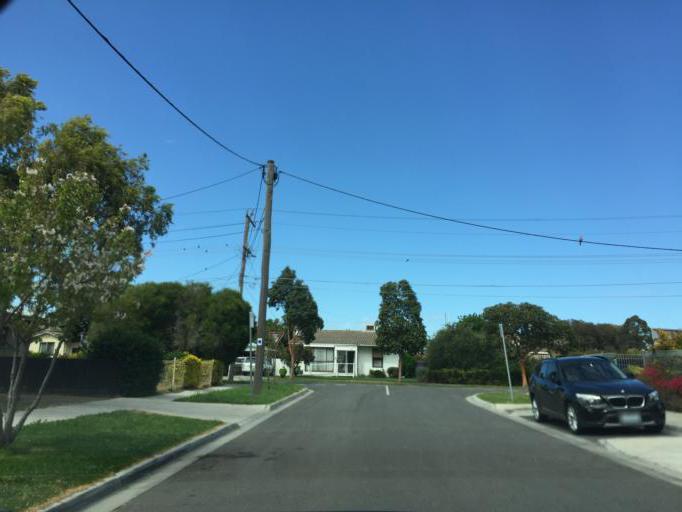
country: AU
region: Victoria
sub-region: Maribyrnong
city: Braybrook
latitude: -37.7845
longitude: 144.8579
